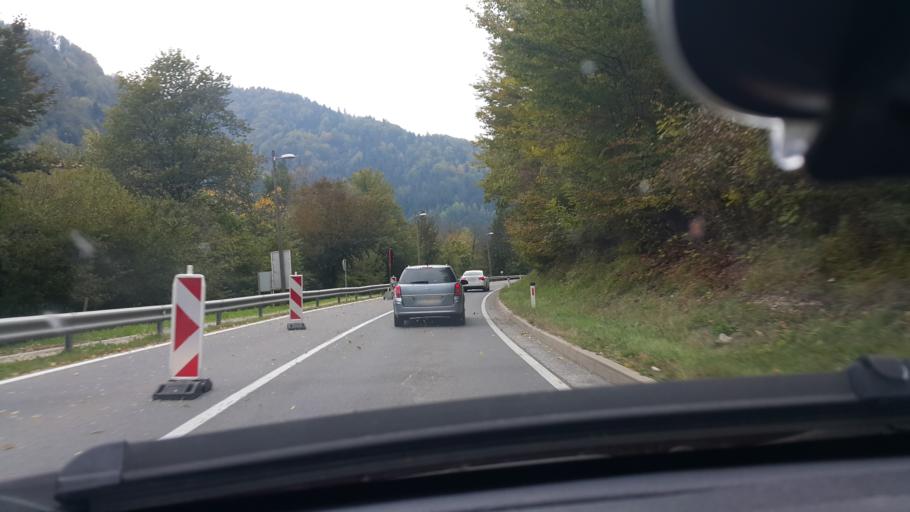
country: SI
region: Podvelka
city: Podvelka
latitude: 46.5904
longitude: 15.3262
